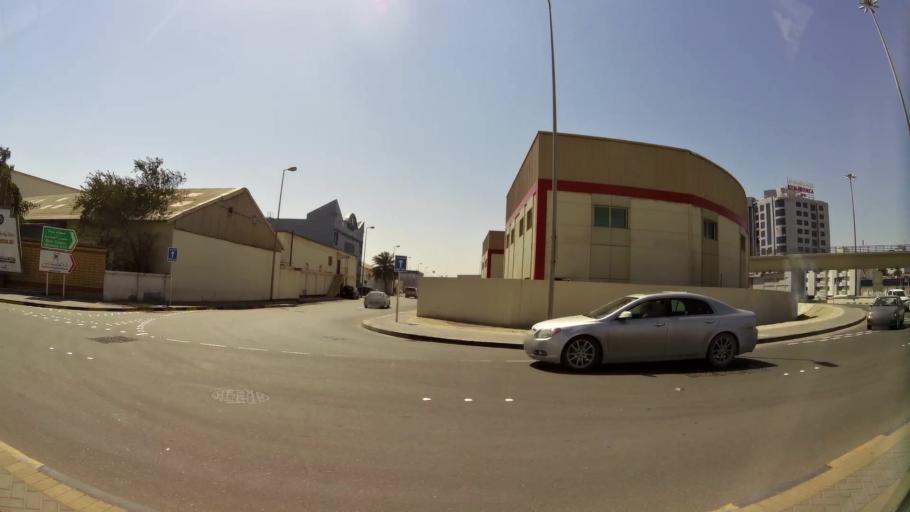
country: BH
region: Manama
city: Manama
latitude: 26.2023
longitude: 50.6028
